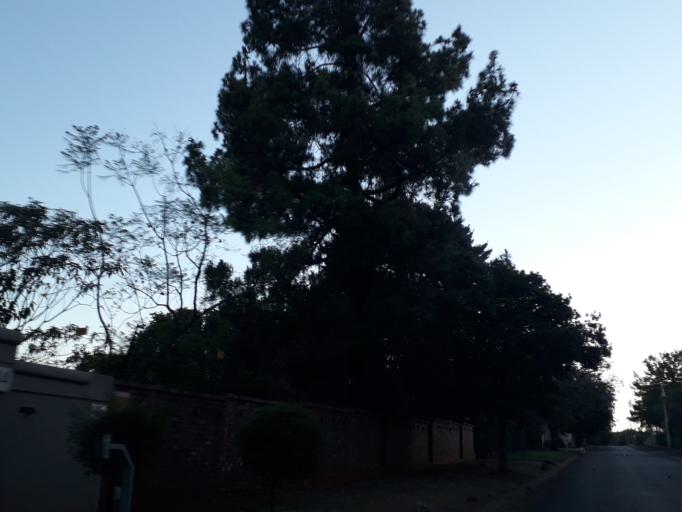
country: ZA
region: Gauteng
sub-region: City of Johannesburg Metropolitan Municipality
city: Roodepoort
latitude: -26.1354
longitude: 27.9394
